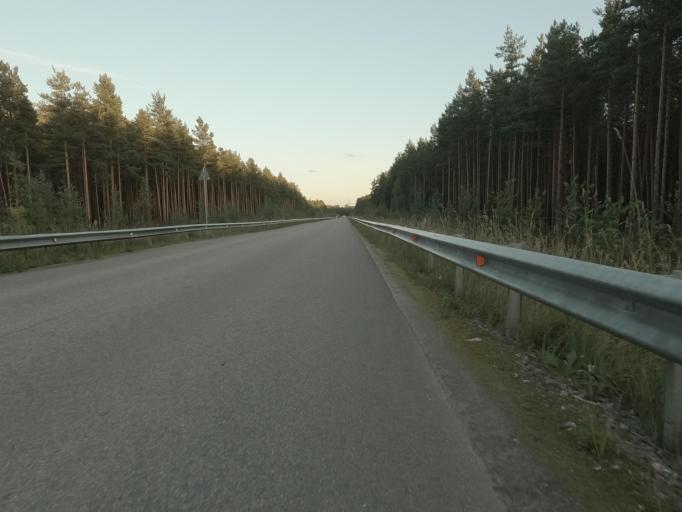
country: RU
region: Leningrad
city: Mga
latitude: 59.7659
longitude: 31.0343
